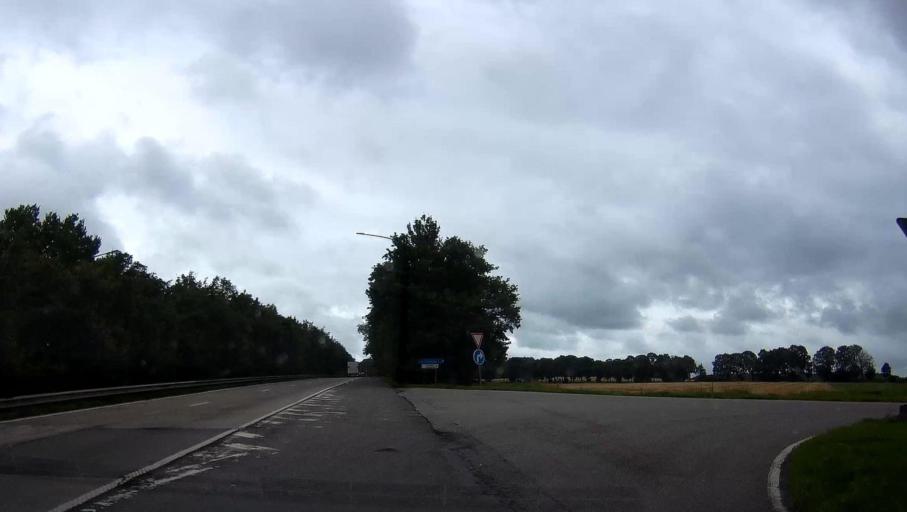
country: BE
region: Wallonia
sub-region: Province de Namur
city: Philippeville
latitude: 50.2326
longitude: 4.5114
